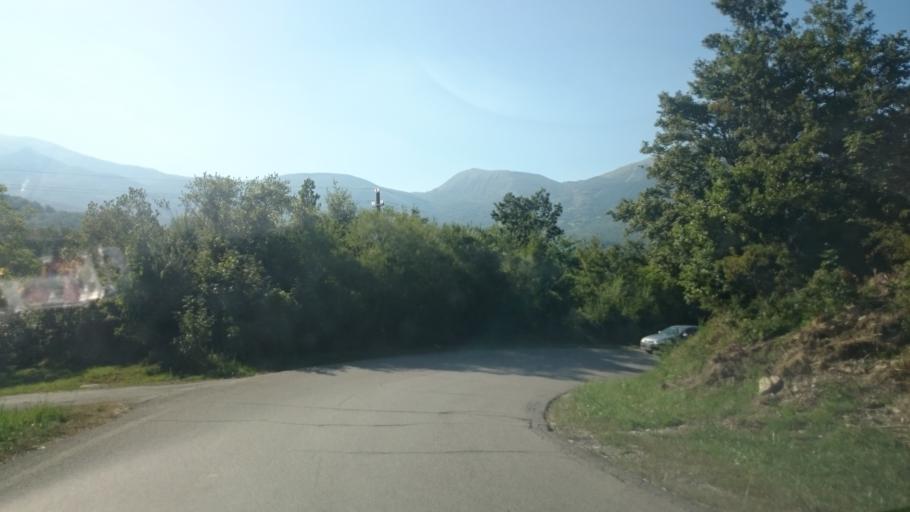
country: IT
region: Emilia-Romagna
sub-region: Provincia di Reggio Emilia
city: Villa Minozzo
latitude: 44.2989
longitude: 10.4575
